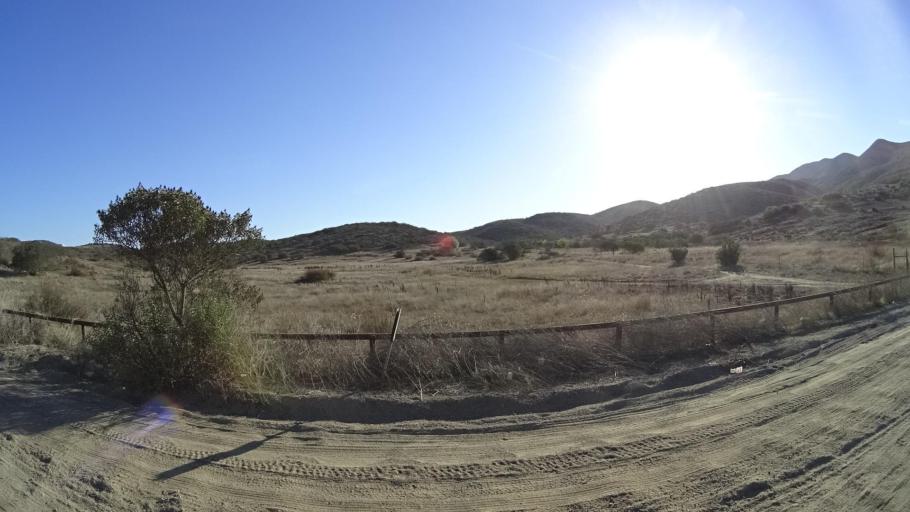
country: US
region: California
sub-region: San Diego County
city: Jamul
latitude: 32.6940
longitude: -116.9030
